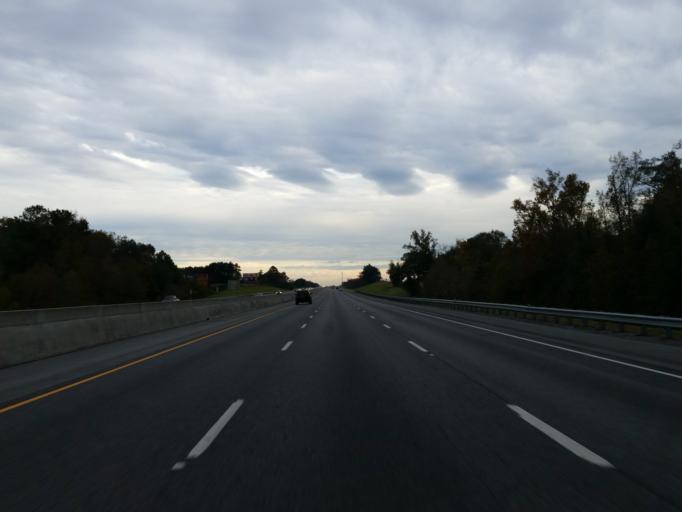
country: US
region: Georgia
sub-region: Lowndes County
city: Hahira
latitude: 30.9700
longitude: -83.3813
